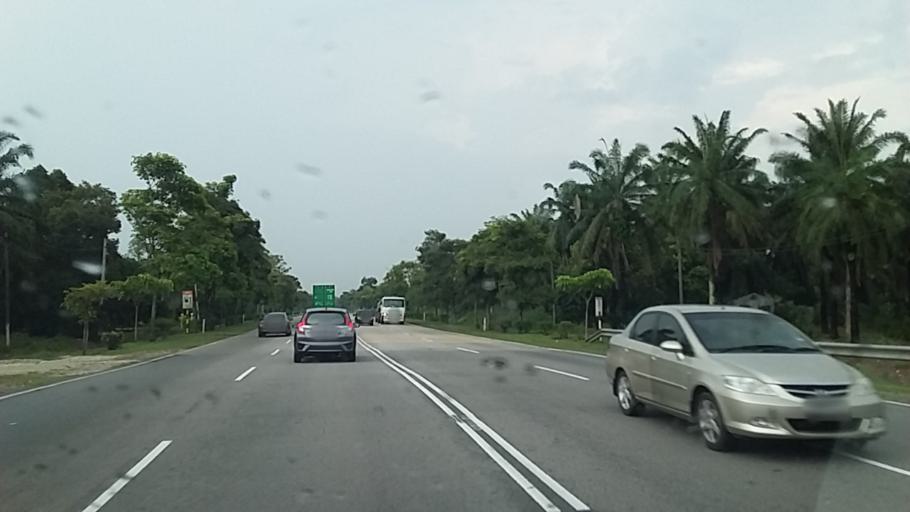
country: MY
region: Johor
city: Parit Raja
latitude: 1.8784
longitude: 103.1448
